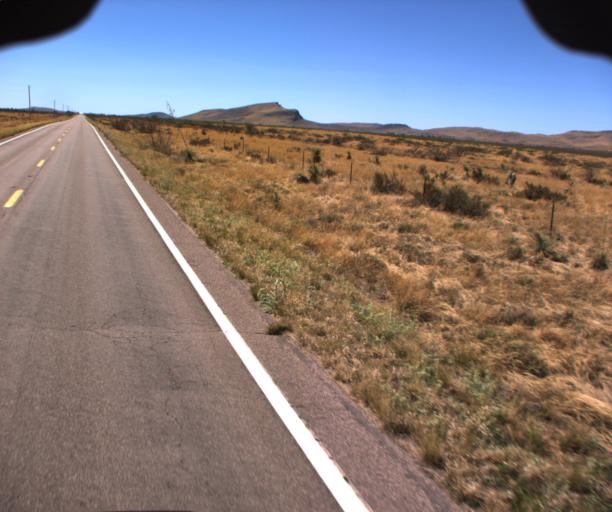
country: US
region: Arizona
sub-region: Cochise County
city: Douglas
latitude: 31.7096
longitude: -109.1196
